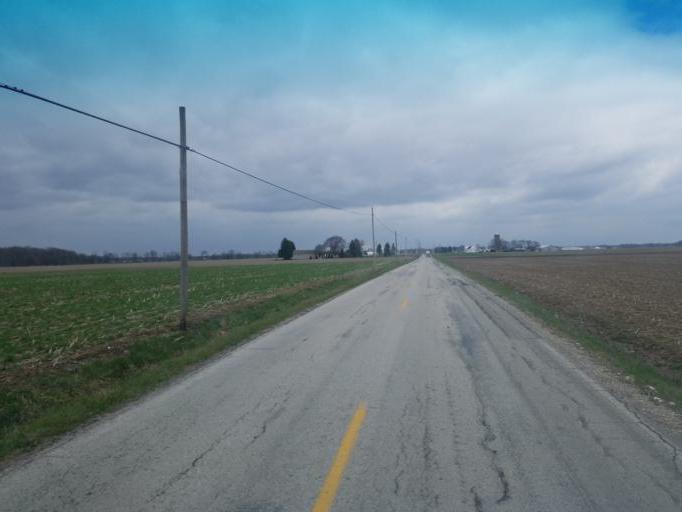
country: US
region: Ohio
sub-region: Marion County
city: Prospect
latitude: 40.4548
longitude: -83.1558
